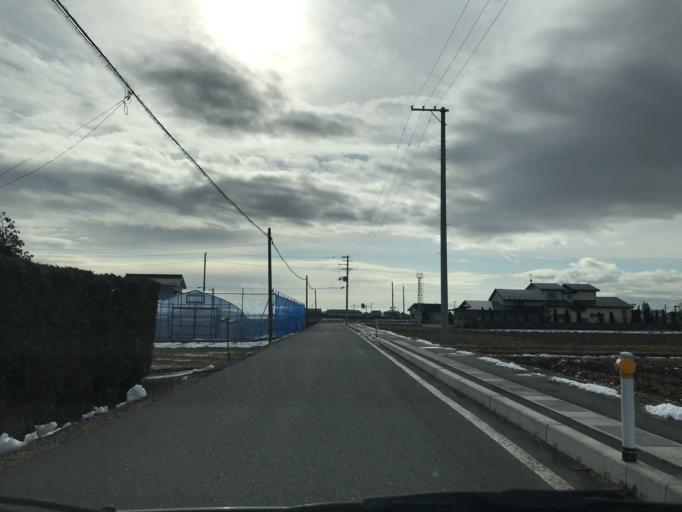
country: JP
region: Iwate
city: Mizusawa
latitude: 39.1776
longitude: 141.1331
